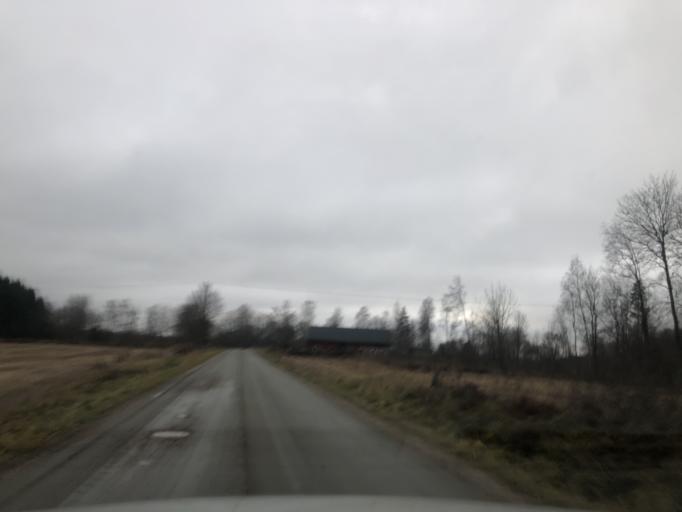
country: SE
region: Vaestra Goetaland
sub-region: Ulricehamns Kommun
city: Ulricehamn
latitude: 57.8823
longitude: 13.4076
